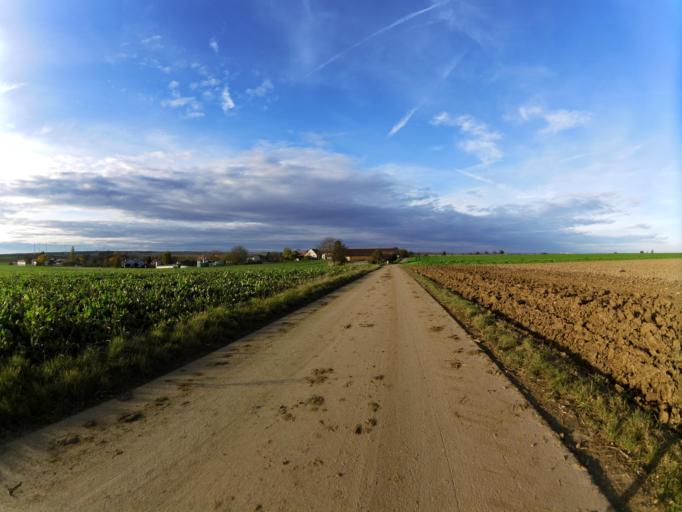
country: DE
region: Bavaria
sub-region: Regierungsbezirk Unterfranken
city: Geroldshausen
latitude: 49.6901
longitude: 9.9360
